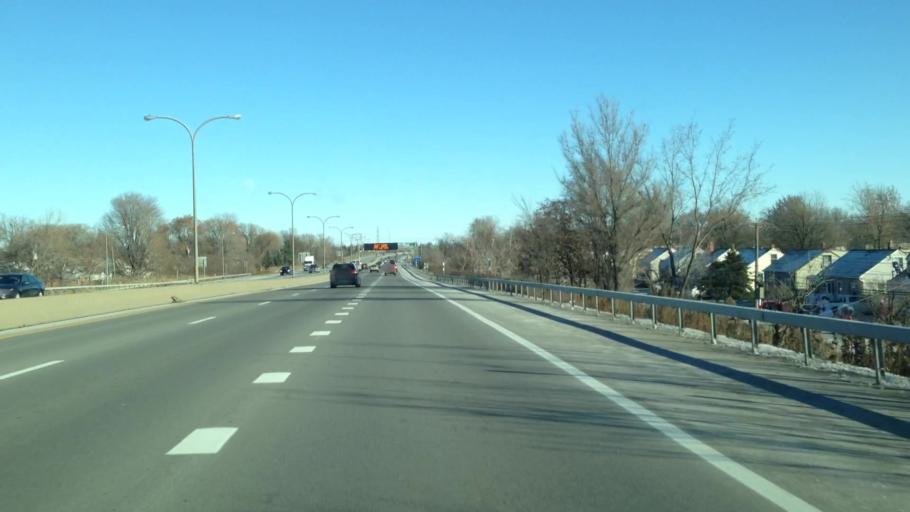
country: US
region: New York
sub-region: Erie County
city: Eggertsville
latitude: 42.9329
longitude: -78.7831
